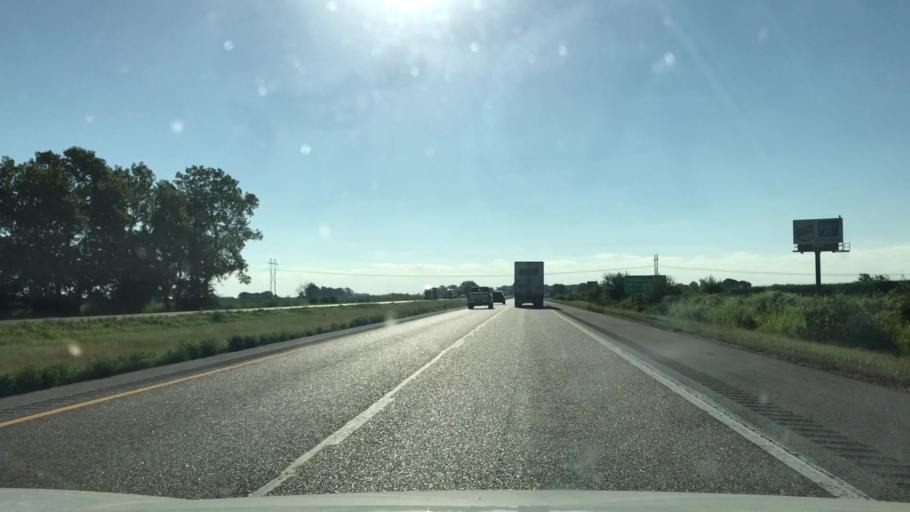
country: US
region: Illinois
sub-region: Saint Clair County
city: Lebanon
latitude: 38.5505
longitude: -89.7897
